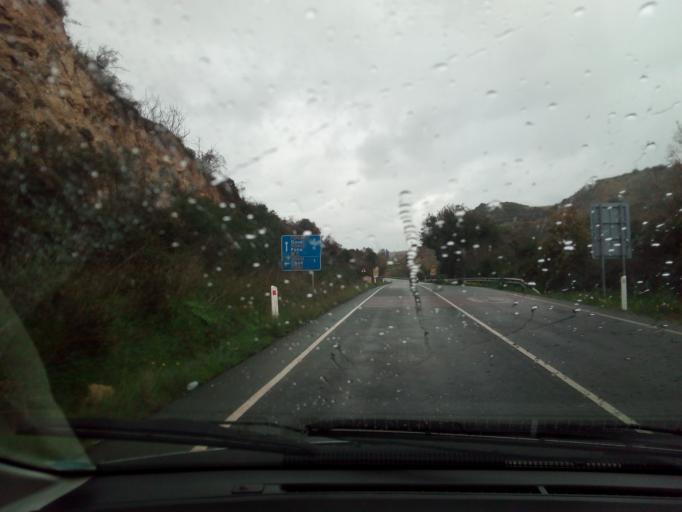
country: CY
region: Pafos
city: Polis
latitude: 34.9746
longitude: 32.4505
